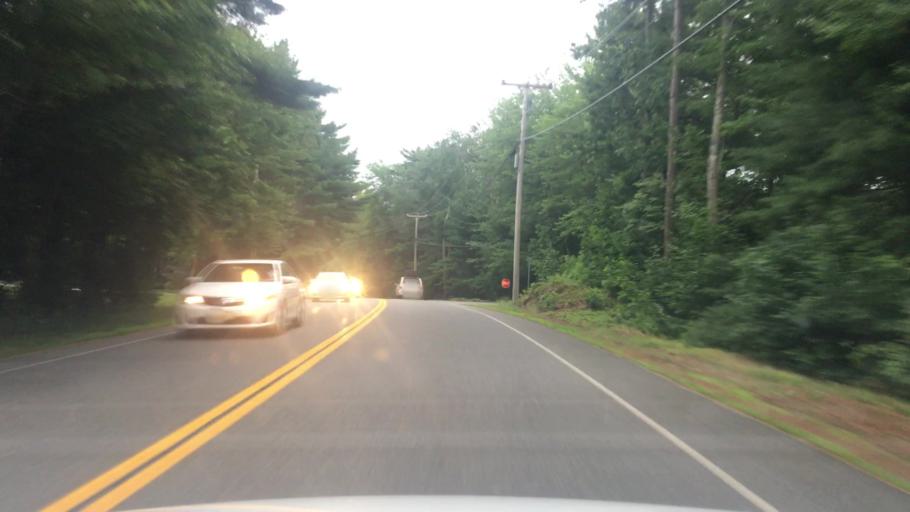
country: US
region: Maine
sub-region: York County
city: Wells Beach Station
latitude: 43.3189
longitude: -70.6005
